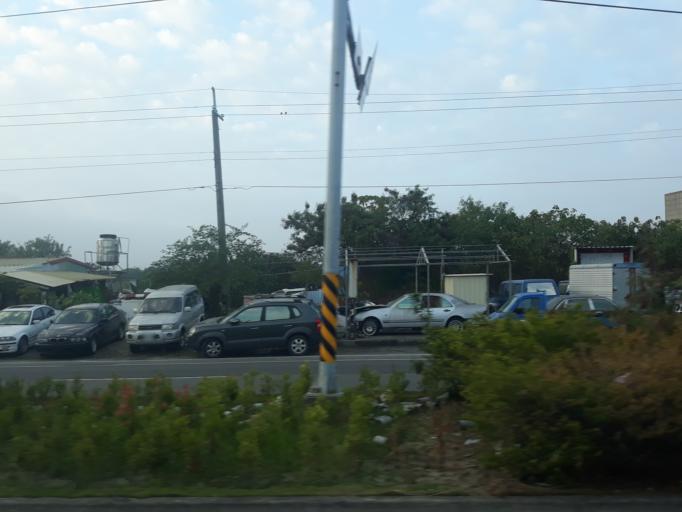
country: TW
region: Taiwan
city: Xinying
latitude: 23.1818
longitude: 120.2347
